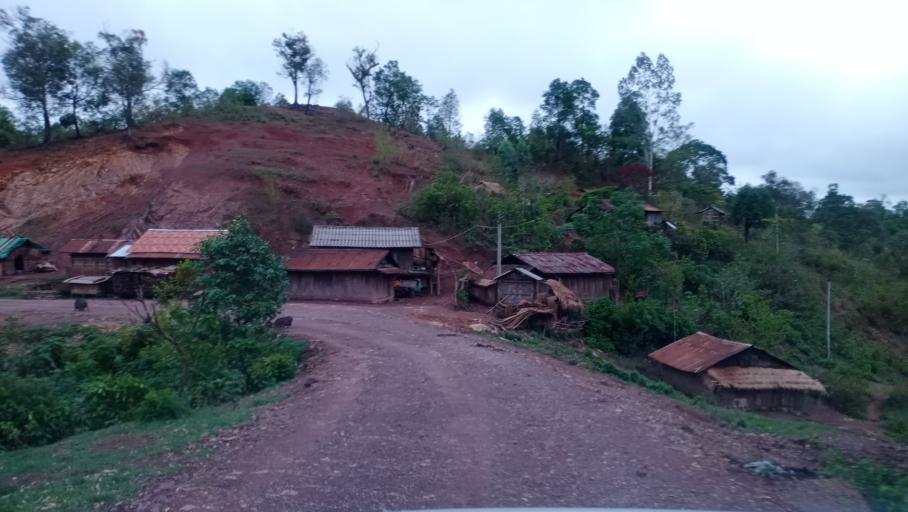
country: LA
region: Phongsali
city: Phongsali
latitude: 21.3387
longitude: 102.0791
